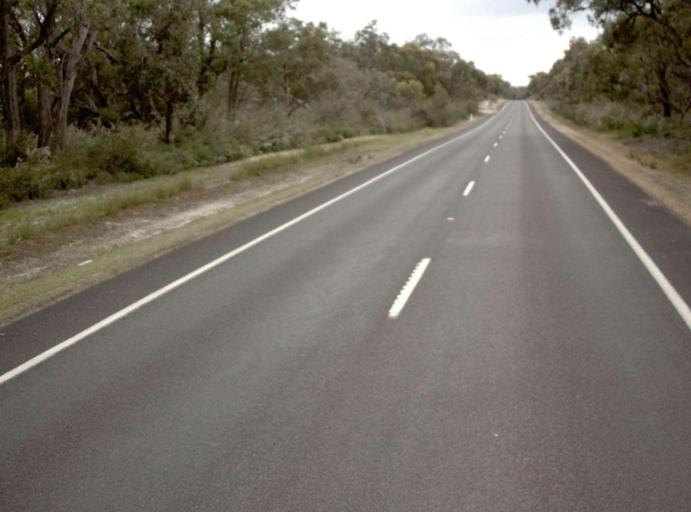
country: AU
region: Victoria
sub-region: Wellington
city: Sale
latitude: -38.3355
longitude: 147.0135
